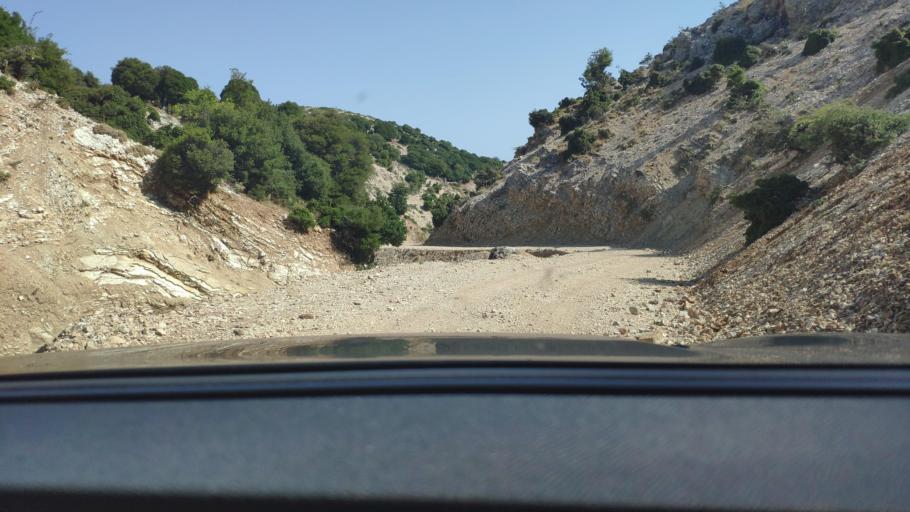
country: GR
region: West Greece
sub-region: Nomos Aitolias kai Akarnanias
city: Monastirakion
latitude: 38.8019
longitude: 20.9966
